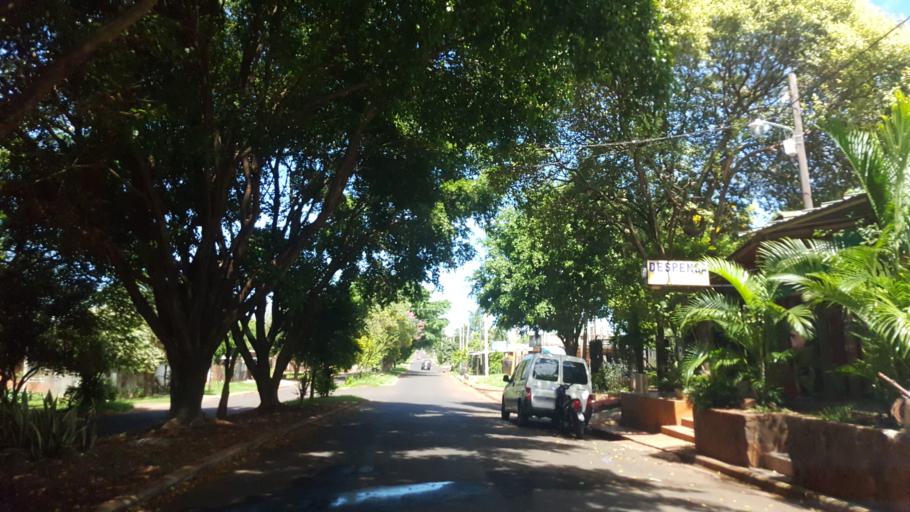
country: AR
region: Misiones
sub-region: Departamento de Capital
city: Posadas
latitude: -27.3796
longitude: -55.9221
